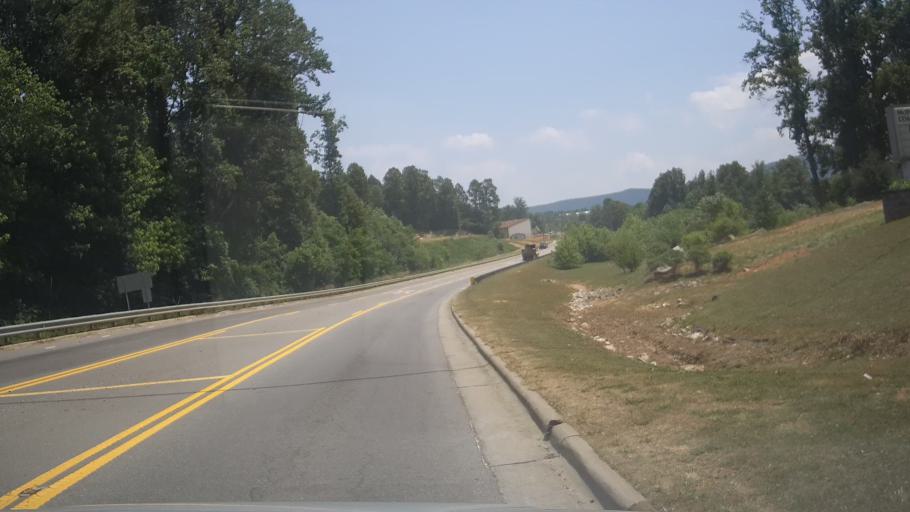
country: US
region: North Carolina
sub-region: McDowell County
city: Marion
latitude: 35.6573
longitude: -81.9609
